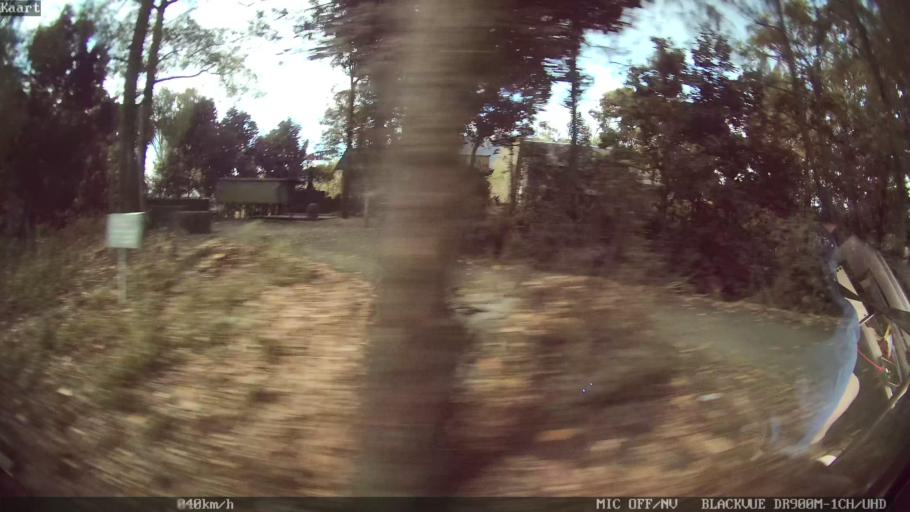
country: ID
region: Bali
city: Banjar Kedisan
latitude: -8.2470
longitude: 115.3481
